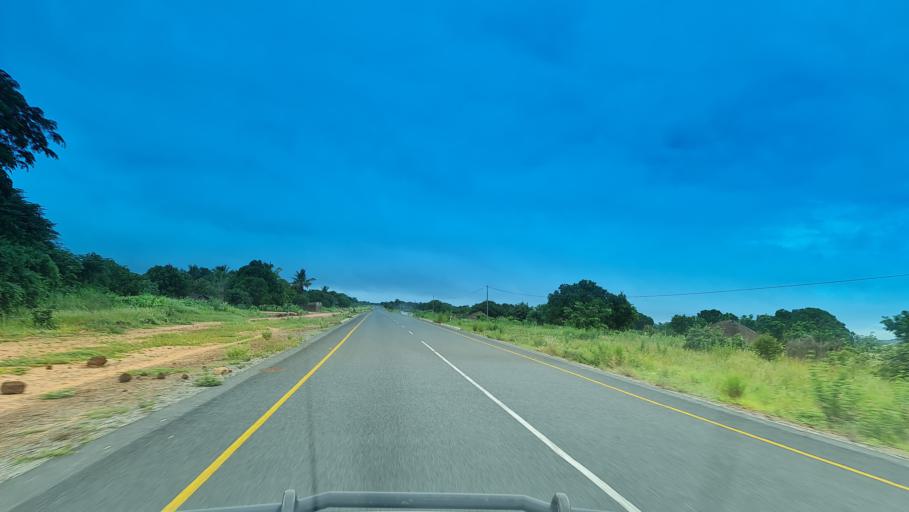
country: MZ
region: Nampula
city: Nampula
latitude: -15.5830
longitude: 39.3240
